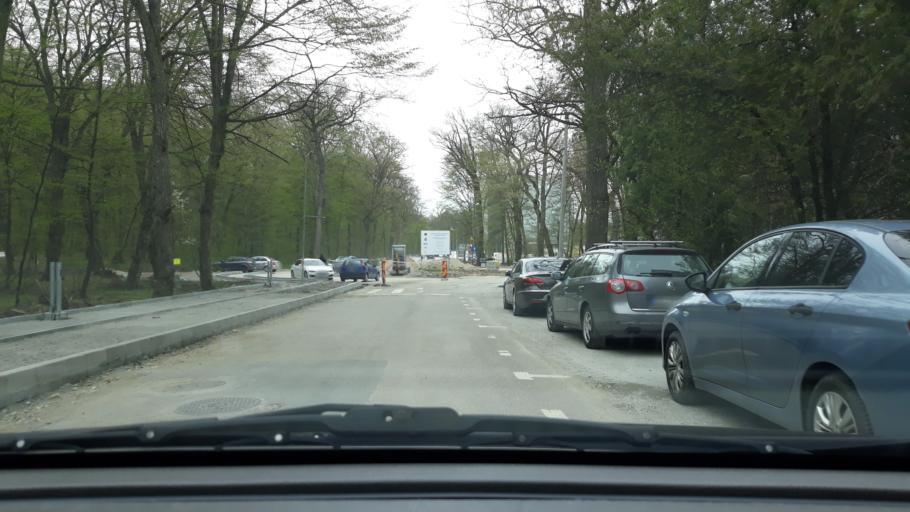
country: RO
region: Bihor
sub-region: Comuna Sanmartin
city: Sanmartin
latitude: 46.9870
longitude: 21.9765
